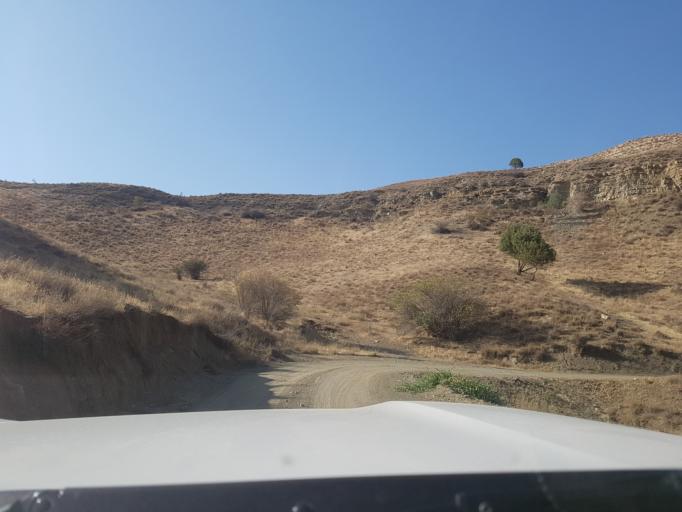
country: TM
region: Balkan
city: Magtymguly
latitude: 38.3001
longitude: 56.7810
